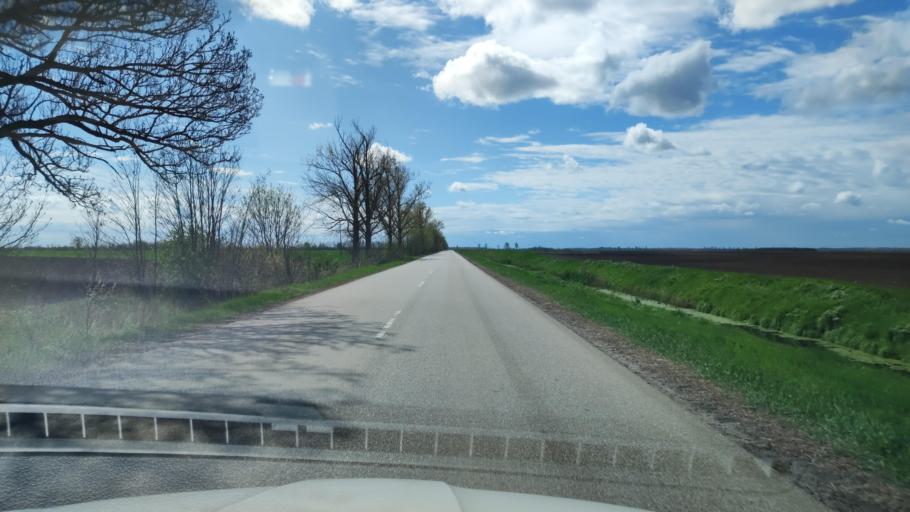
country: HU
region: Pest
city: Abony
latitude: 47.1549
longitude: 20.0072
